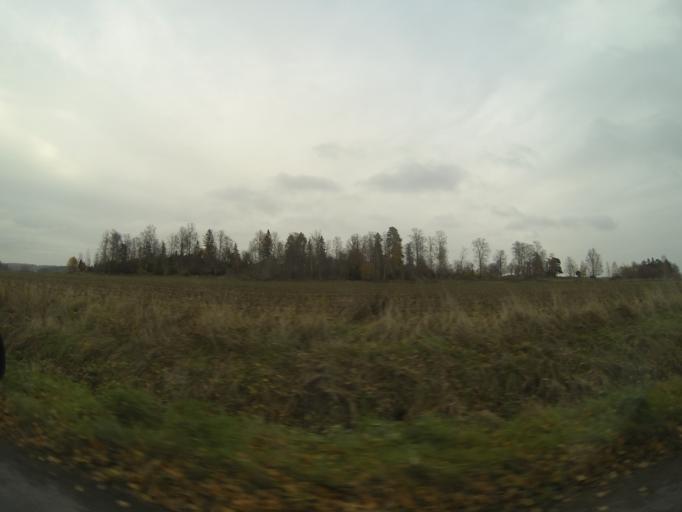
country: SE
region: Vaestmanland
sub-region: Vasteras
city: Skultuna
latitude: 59.6778
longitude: 16.4496
